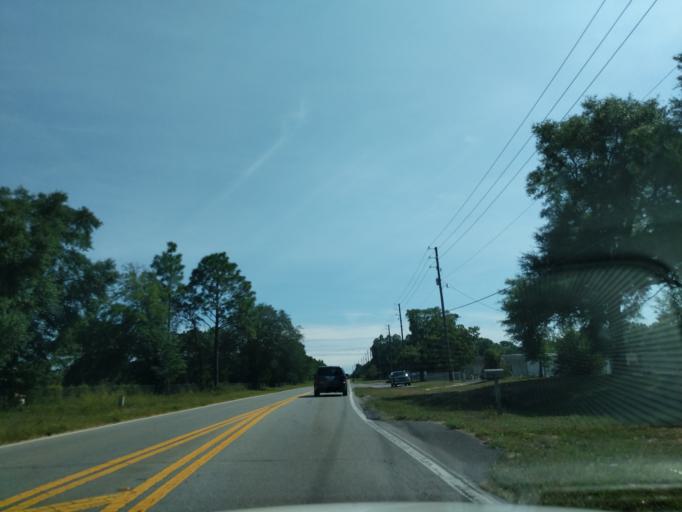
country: US
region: Florida
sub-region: Okaloosa County
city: Crestview
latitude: 30.7248
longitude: -86.6158
